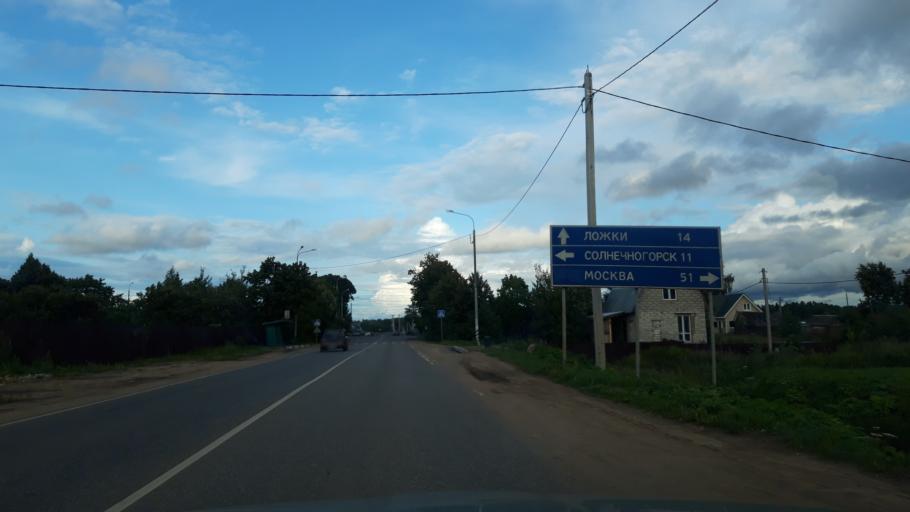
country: RU
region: Moskovskaya
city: Solnechnogorsk
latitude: 56.0931
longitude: 36.9101
